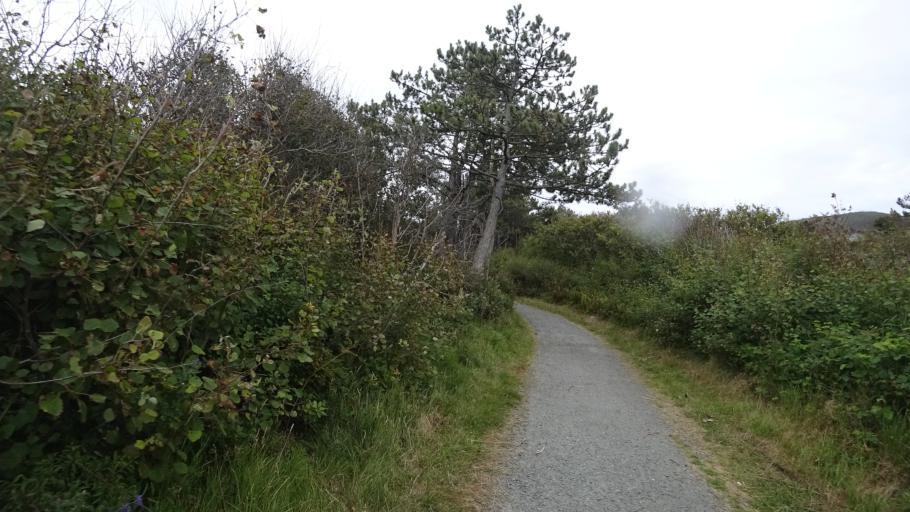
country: SE
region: Vaestra Goetaland
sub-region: Ockero Kommun
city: Hono
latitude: 57.7002
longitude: 11.6201
